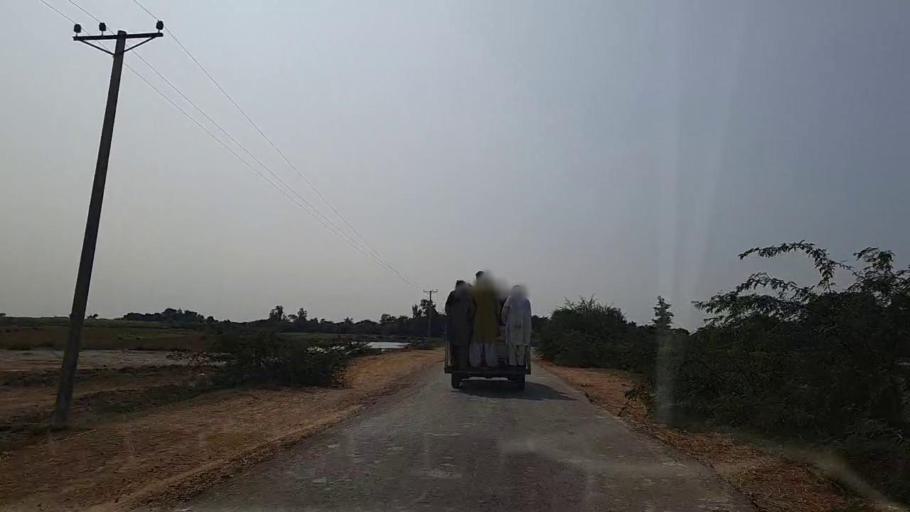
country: PK
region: Sindh
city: Chuhar Jamali
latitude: 24.3721
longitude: 67.9671
